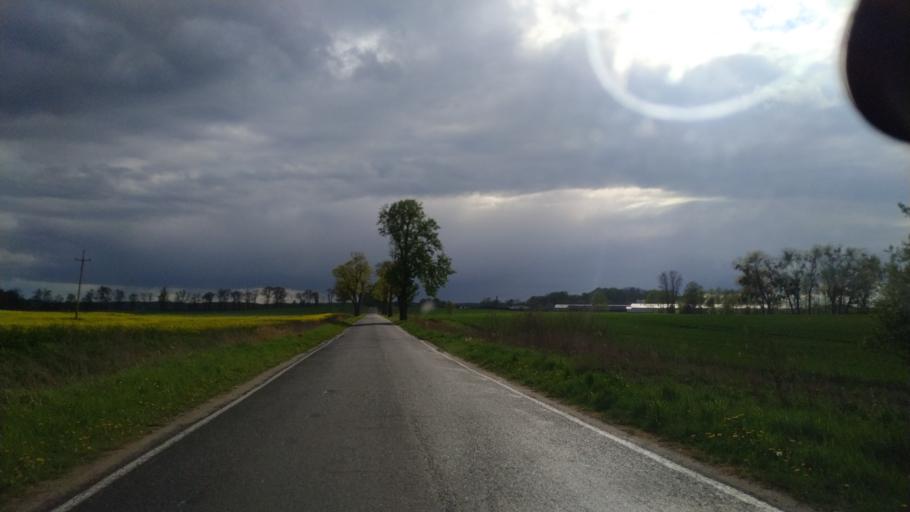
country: PL
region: Pomeranian Voivodeship
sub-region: Powiat starogardzki
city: Smetowo Graniczne
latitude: 53.7233
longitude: 18.6237
